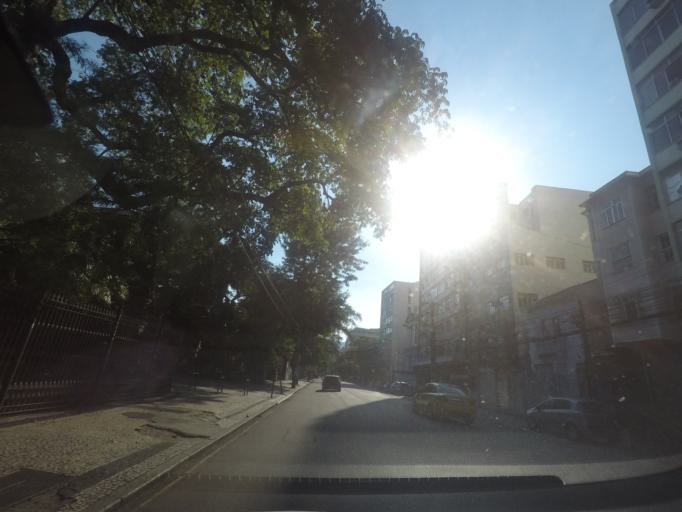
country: BR
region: Rio de Janeiro
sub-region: Rio De Janeiro
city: Rio de Janeiro
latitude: -22.9133
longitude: -43.2172
